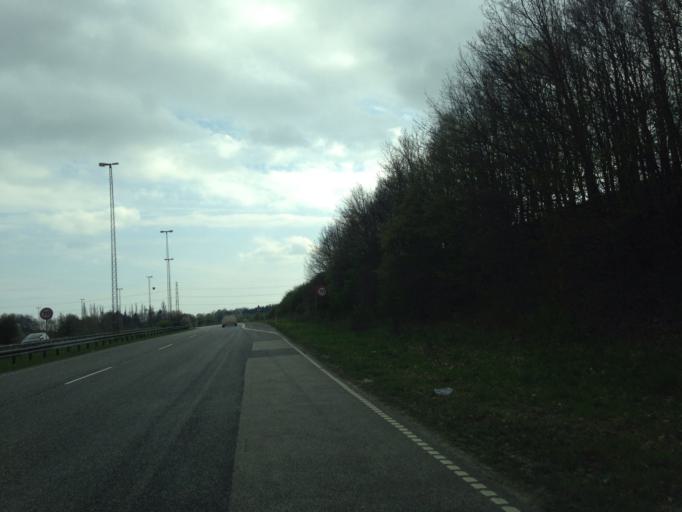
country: DK
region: Capital Region
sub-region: Hoje-Taastrup Kommune
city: Taastrup
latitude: 55.6389
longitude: 12.2807
